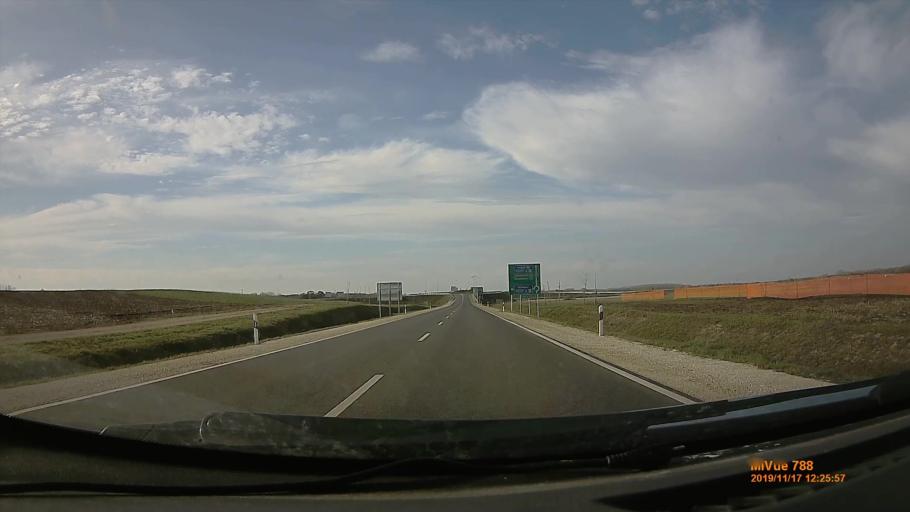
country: HU
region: Bacs-Kiskun
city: Kecskemet
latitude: 46.9320
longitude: 19.6246
